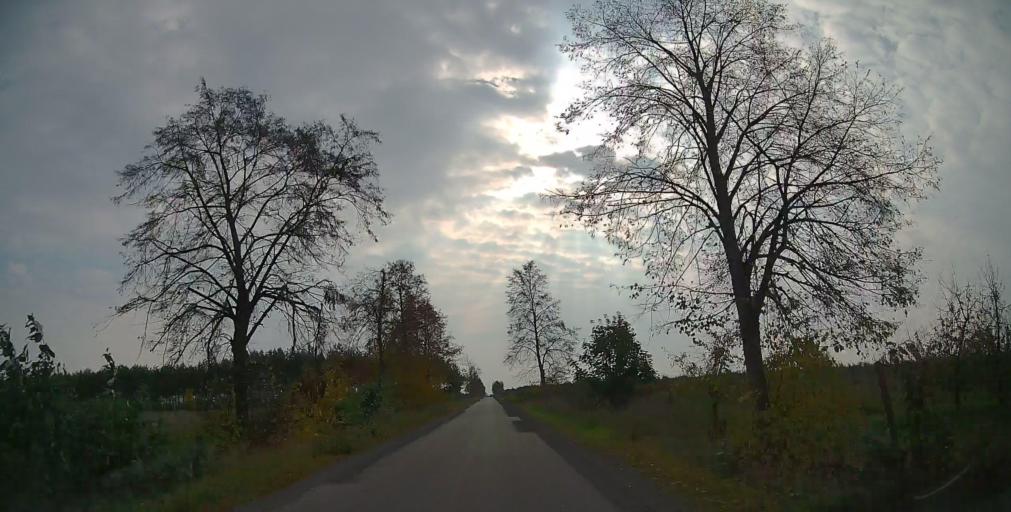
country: PL
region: Masovian Voivodeship
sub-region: Powiat grojecki
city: Mogielnica
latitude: 51.6548
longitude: 20.7205
